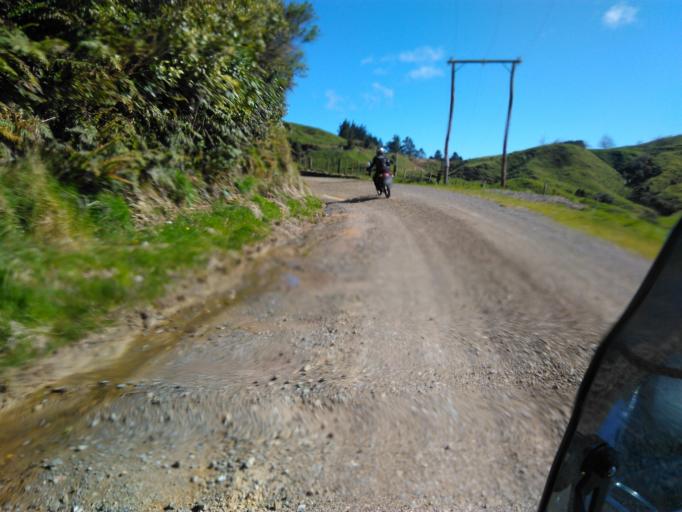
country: NZ
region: Bay of Plenty
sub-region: Opotiki District
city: Opotiki
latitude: -38.3387
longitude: 177.5811
